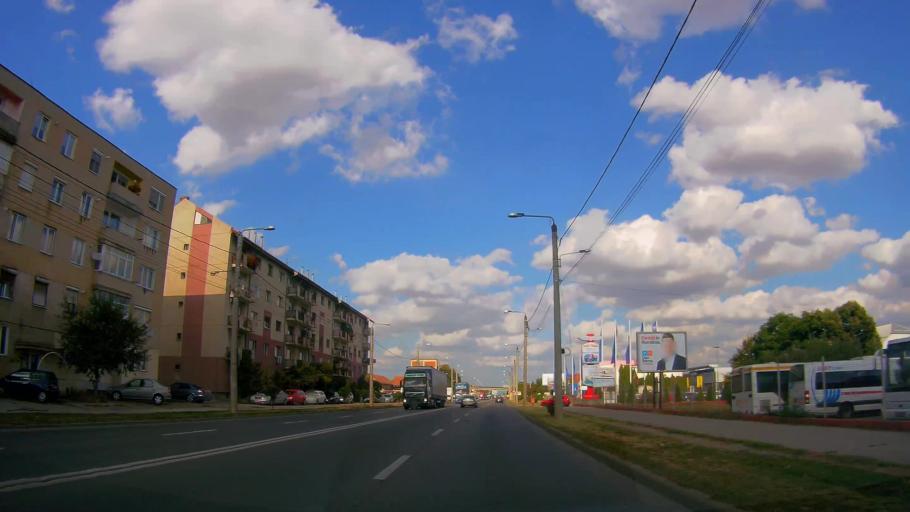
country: RO
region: Satu Mare
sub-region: Municipiul Satu Mare
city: Satu Mare
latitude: 47.7922
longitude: 22.8926
